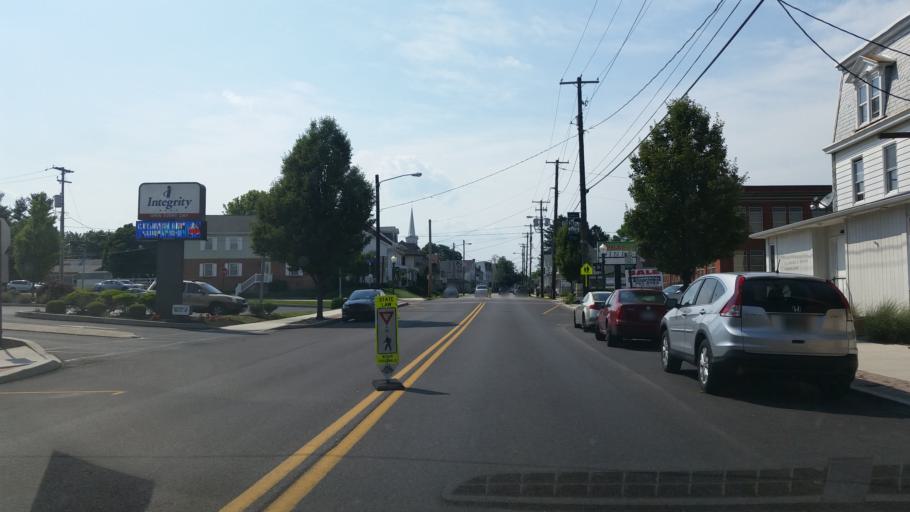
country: US
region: Pennsylvania
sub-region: Cumberland County
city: New Cumberland
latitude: 40.2280
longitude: -76.8667
